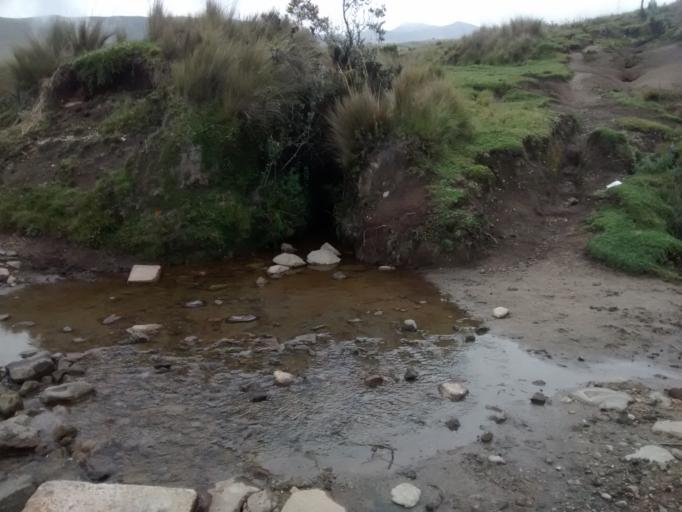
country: EC
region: Pichincha
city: Quito
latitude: -0.1830
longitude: -78.5415
